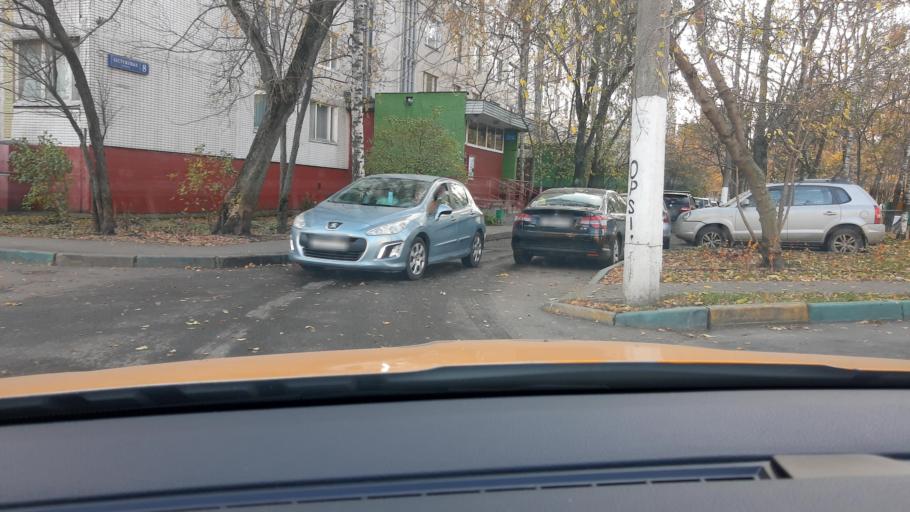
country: RU
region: Moscow
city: Otradnoye
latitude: 55.8697
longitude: 37.6036
